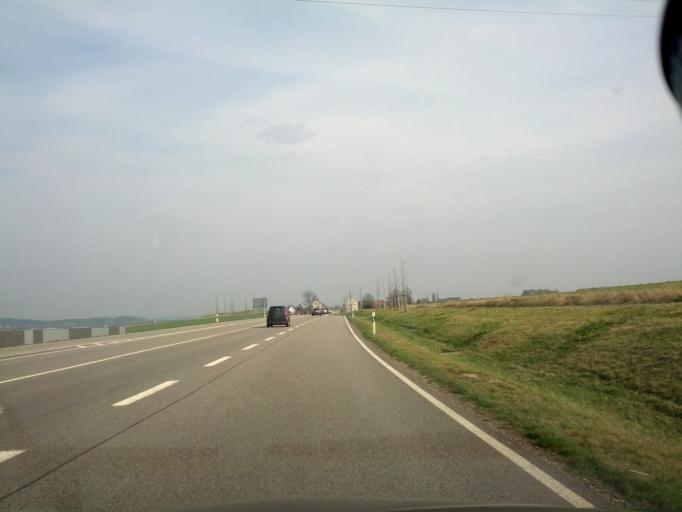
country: DE
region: Saxony
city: Reinsdorf
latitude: 50.6858
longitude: 12.5682
